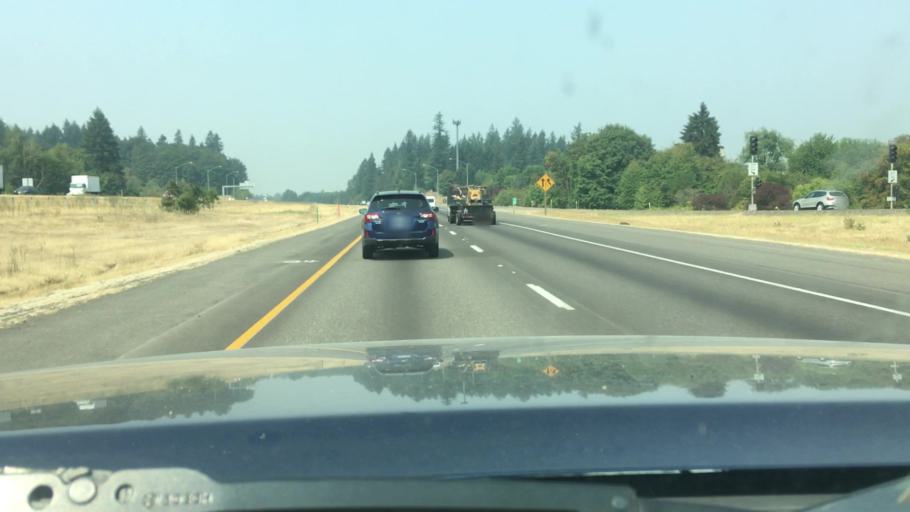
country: US
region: Oregon
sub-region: Clackamas County
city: Stafford
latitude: 45.3709
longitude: -122.7076
